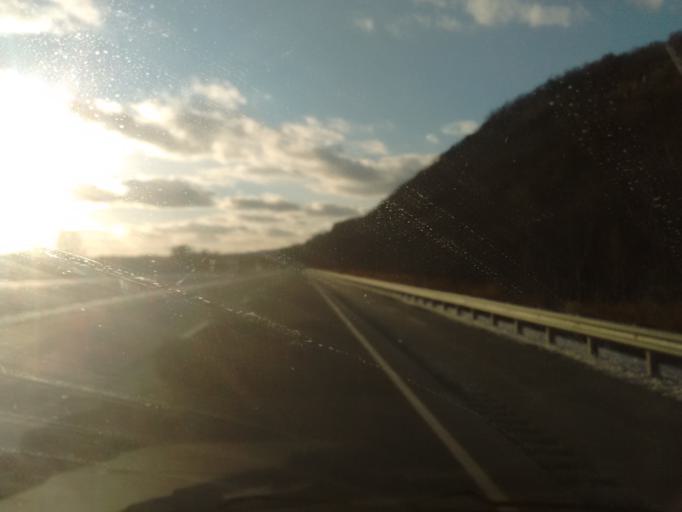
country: US
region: Pennsylvania
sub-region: Pike County
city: Matamoras
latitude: 41.3525
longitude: -74.7347
